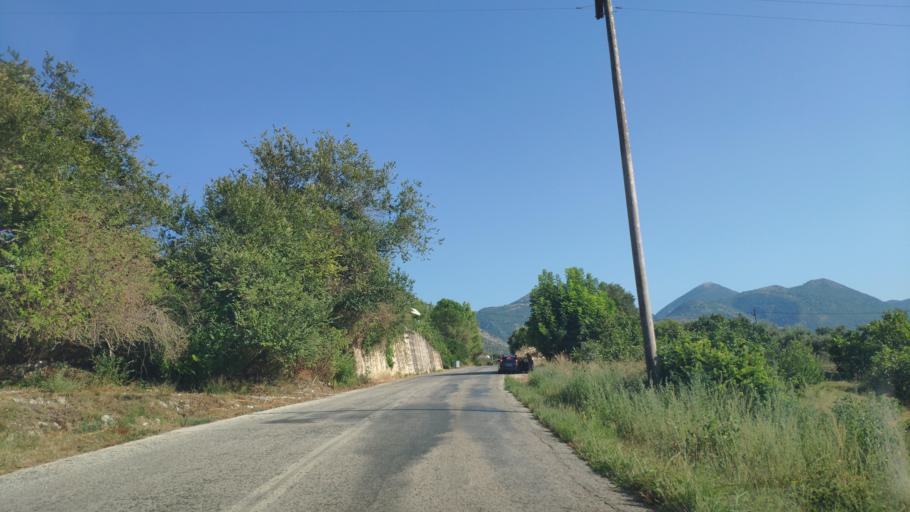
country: GR
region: Epirus
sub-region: Nomos Prevezis
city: Kanalaki
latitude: 39.2644
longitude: 20.6037
